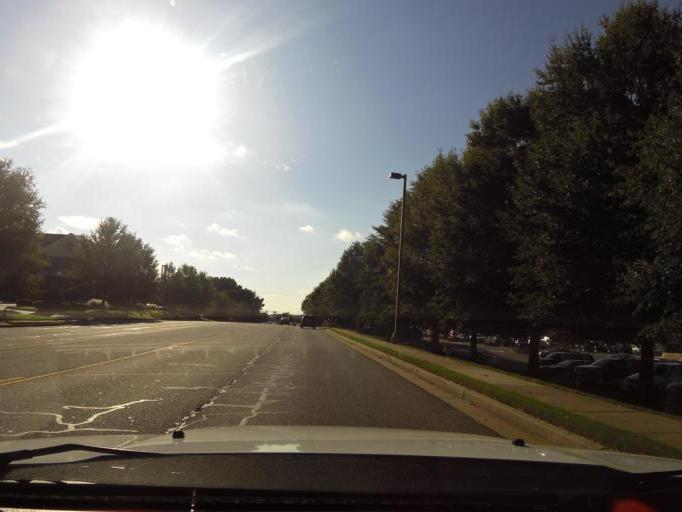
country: US
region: Georgia
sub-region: Cobb County
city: Kennesaw
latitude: 34.0115
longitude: -84.5746
